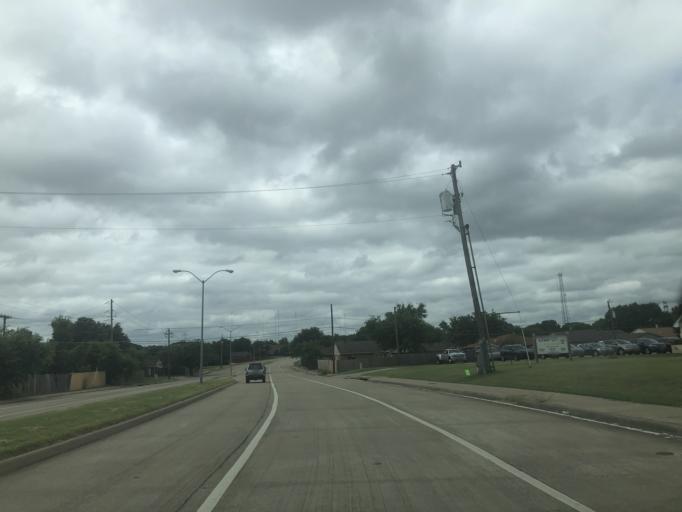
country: US
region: Texas
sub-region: Dallas County
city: Duncanville
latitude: 32.6458
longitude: -96.9523
